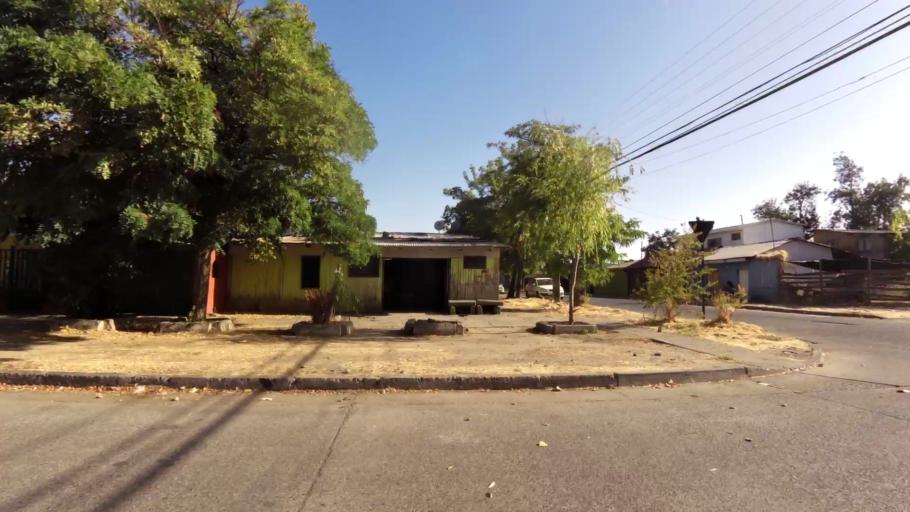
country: CL
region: Maule
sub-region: Provincia de Talca
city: Talca
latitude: -35.4161
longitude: -71.6519
